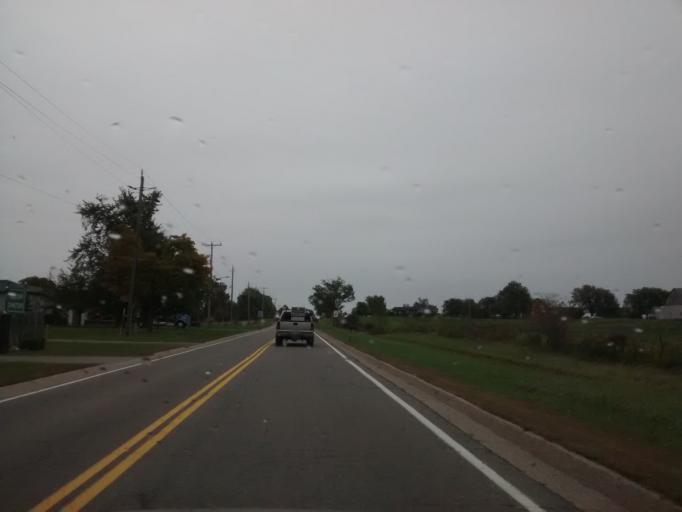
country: CA
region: Ontario
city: Ancaster
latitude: 42.8348
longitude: -79.9242
